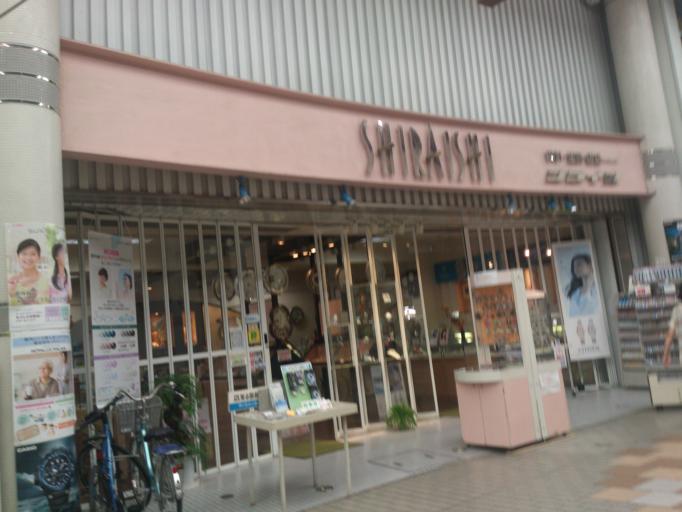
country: JP
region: Yamaguchi
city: Yamaguchi-shi
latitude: 34.1758
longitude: 131.4763
